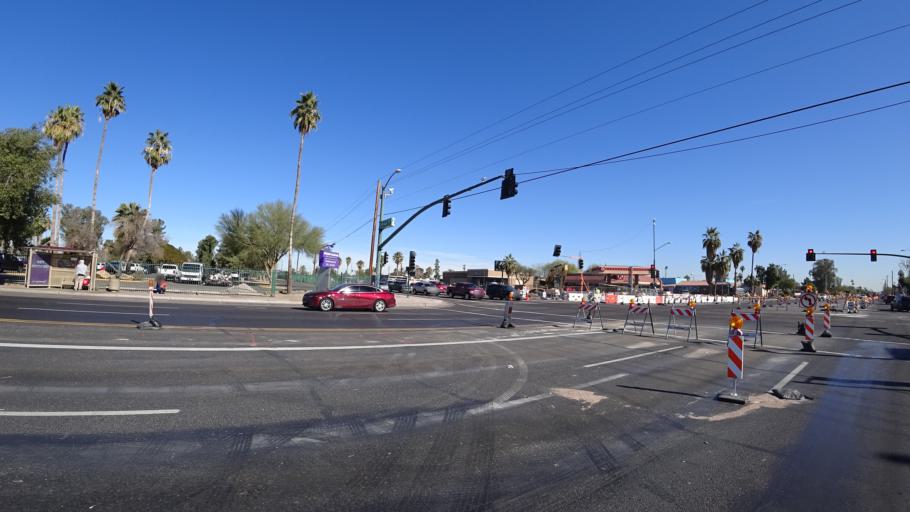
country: US
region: Arizona
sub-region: Maricopa County
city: Glendale
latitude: 33.4950
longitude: -112.1868
